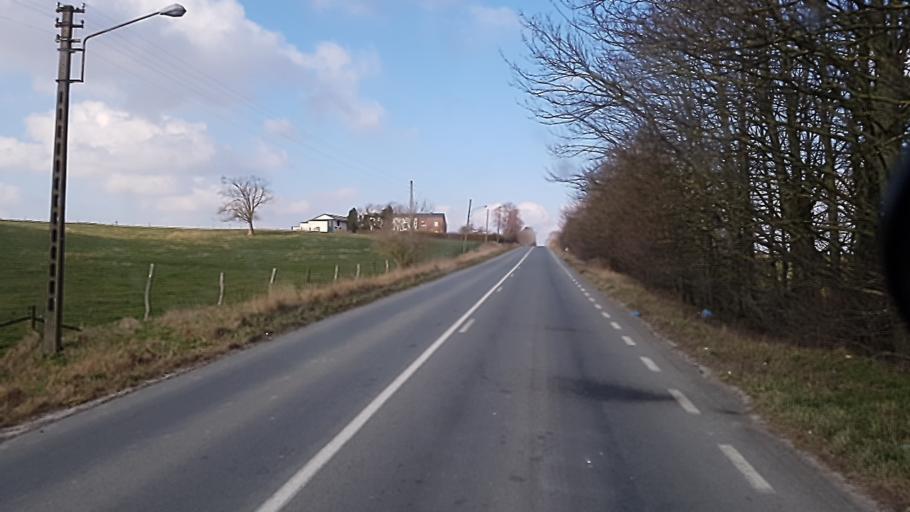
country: BE
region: Wallonia
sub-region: Province du Hainaut
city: Quevy-le-Petit
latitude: 50.3811
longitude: 4.0126
